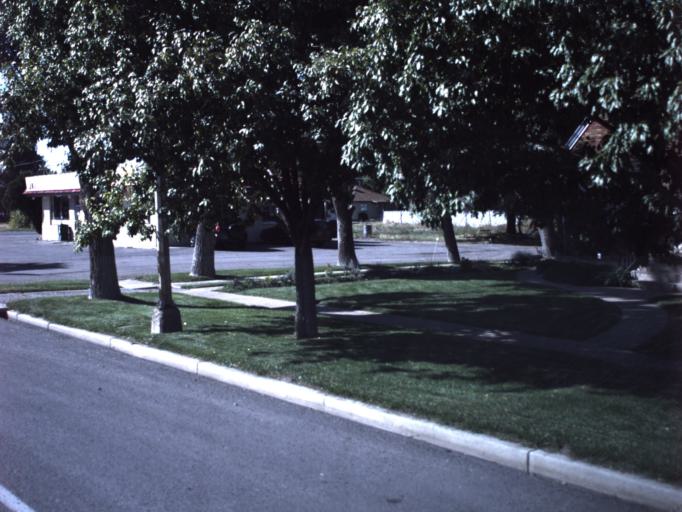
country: US
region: Utah
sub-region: Juab County
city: Nephi
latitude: 39.7035
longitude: -111.8362
